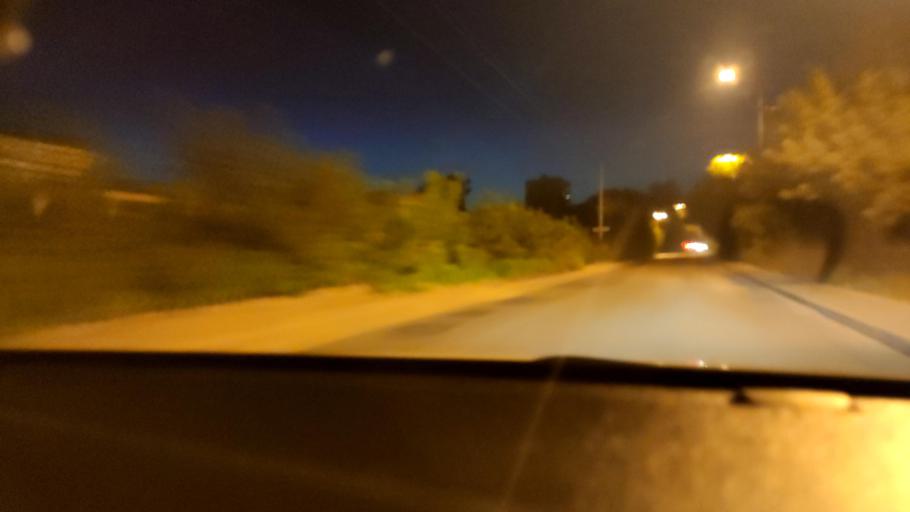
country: RU
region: Tatarstan
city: Vysokaya Gora
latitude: 55.8649
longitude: 49.2364
